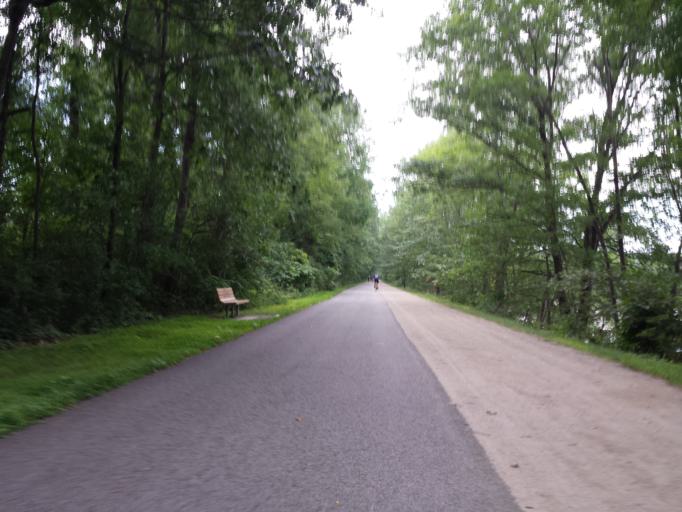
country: US
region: New York
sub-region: Dutchess County
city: Hillside Lake
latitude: 41.5923
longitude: -73.8282
